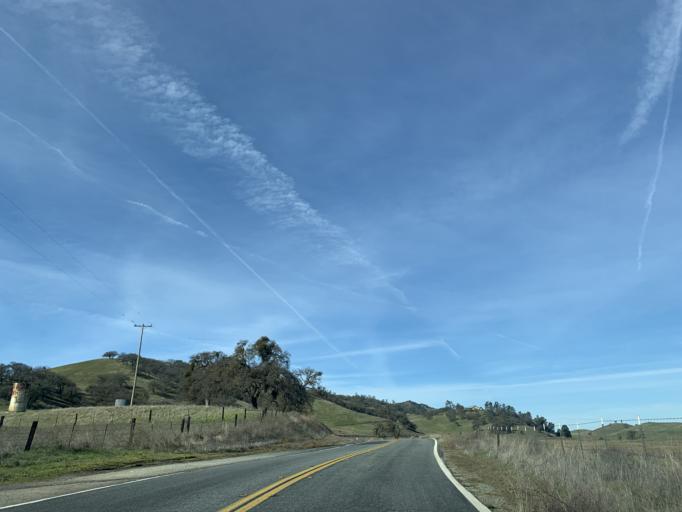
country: US
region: California
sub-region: Monterey County
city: Soledad
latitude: 36.5527
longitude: -121.1662
